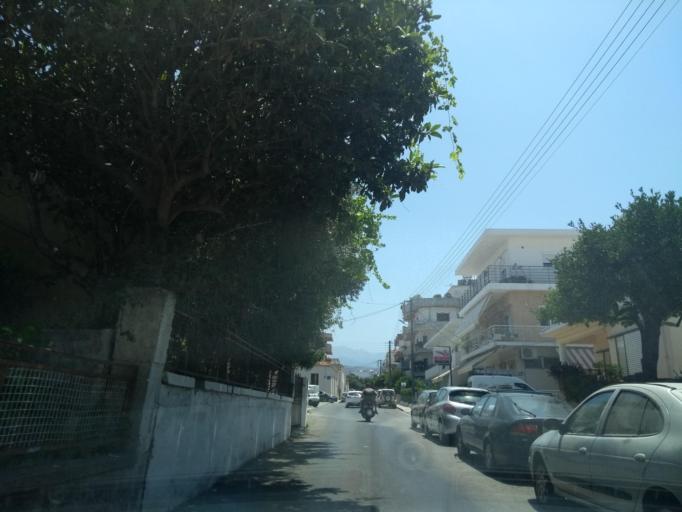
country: GR
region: Crete
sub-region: Nomos Chanias
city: Chania
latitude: 35.5098
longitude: 24.0220
